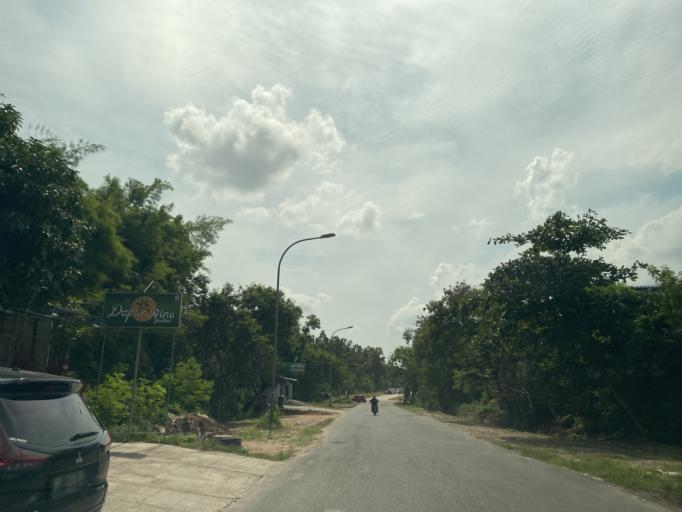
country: SG
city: Singapore
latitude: 1.1277
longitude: 104.0468
